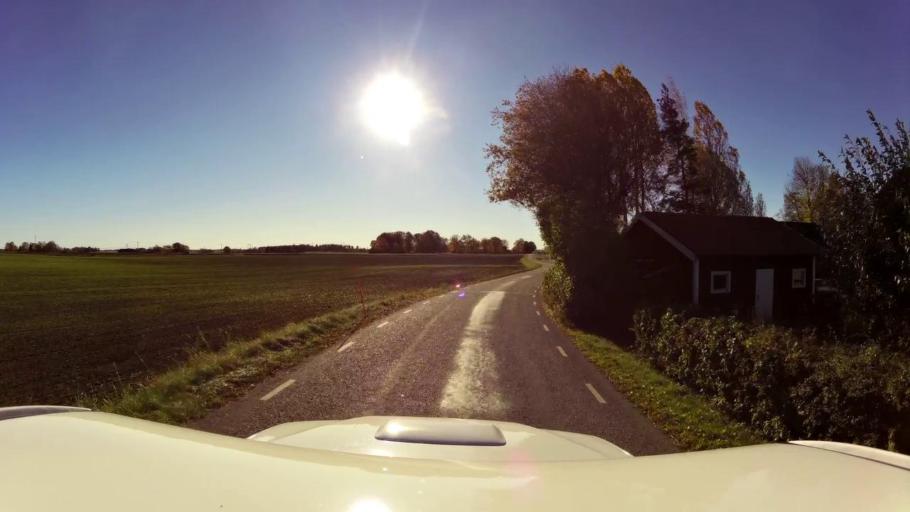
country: SE
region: OEstergoetland
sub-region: Linkopings Kommun
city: Ljungsbro
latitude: 58.4828
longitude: 15.4193
